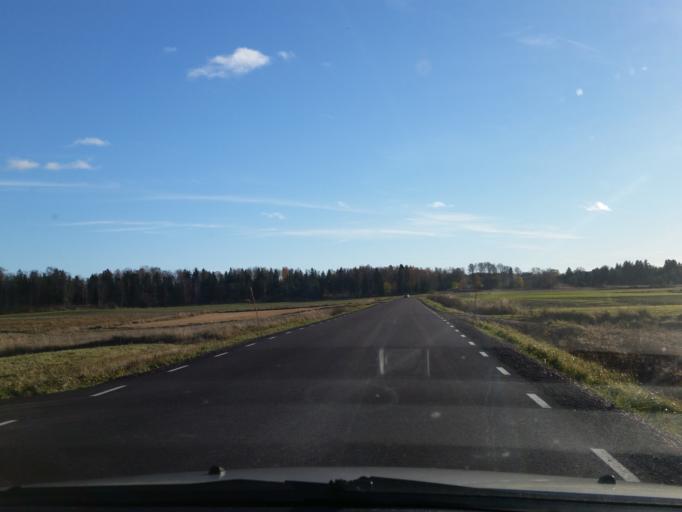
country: AX
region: Alands landsbygd
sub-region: Jomala
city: Jomala
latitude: 60.1957
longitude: 19.9588
